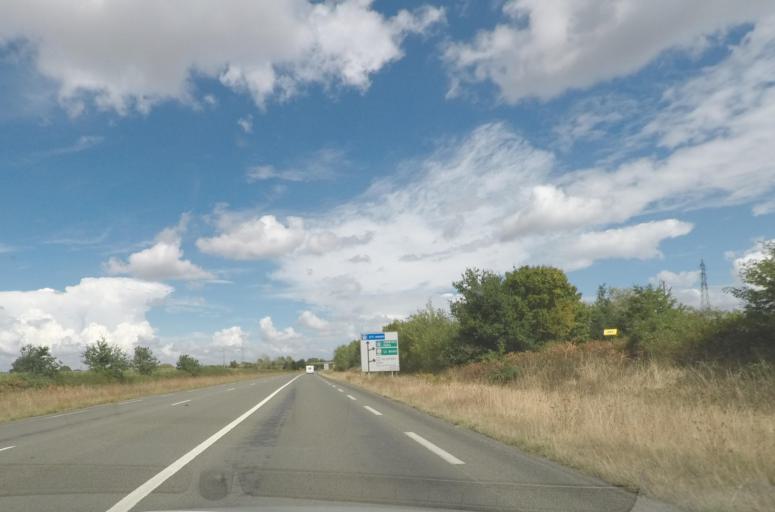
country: FR
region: Pays de la Loire
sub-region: Departement de la Sarthe
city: Spay
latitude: 47.9290
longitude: 0.1610
